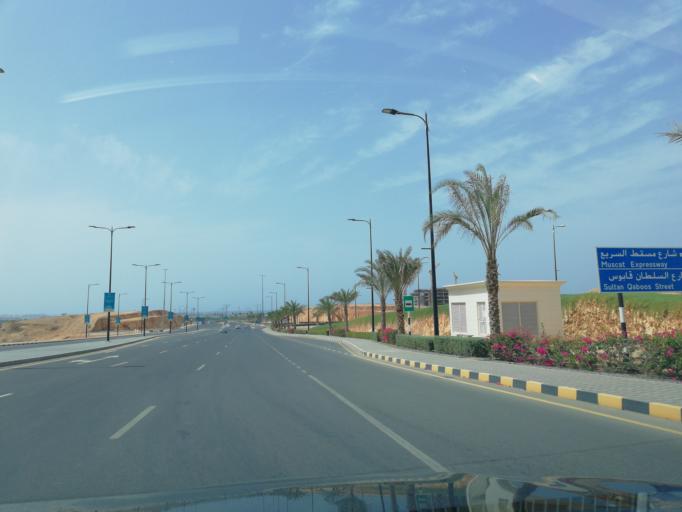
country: OM
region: Muhafazat Masqat
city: Bawshar
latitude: 23.5745
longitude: 58.3249
